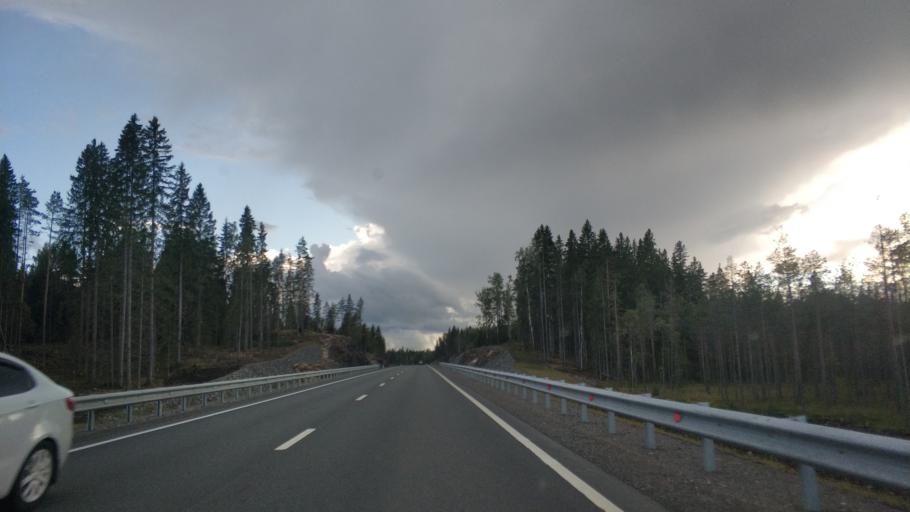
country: RU
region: Republic of Karelia
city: Lakhdenpokh'ya
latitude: 61.4337
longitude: 29.9758
